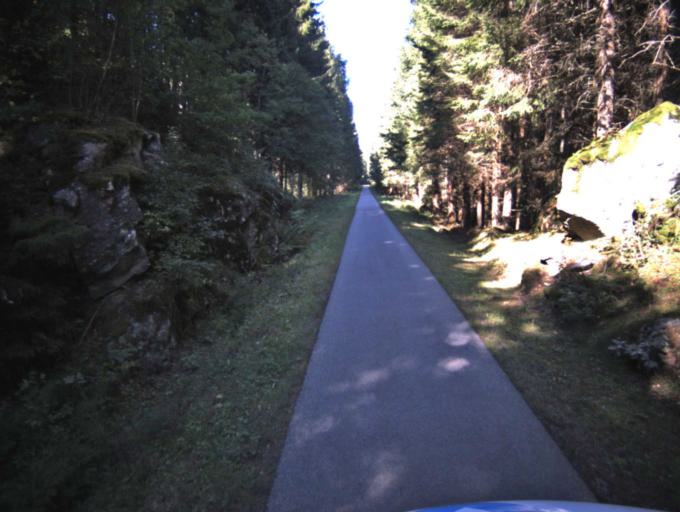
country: SE
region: Vaestra Goetaland
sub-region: Ulricehamns Kommun
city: Ulricehamn
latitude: 57.8187
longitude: 13.3477
